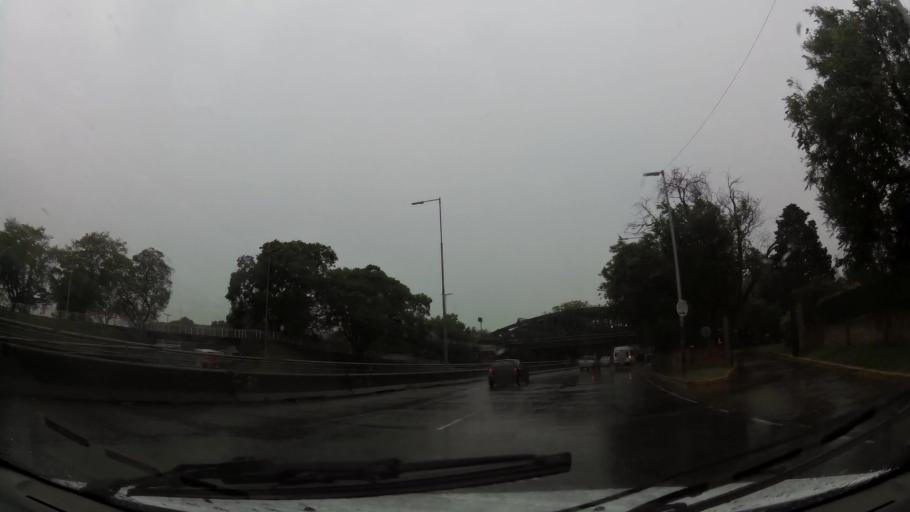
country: AR
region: Buenos Aires F.D.
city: Retiro
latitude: -34.5678
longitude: -58.4085
